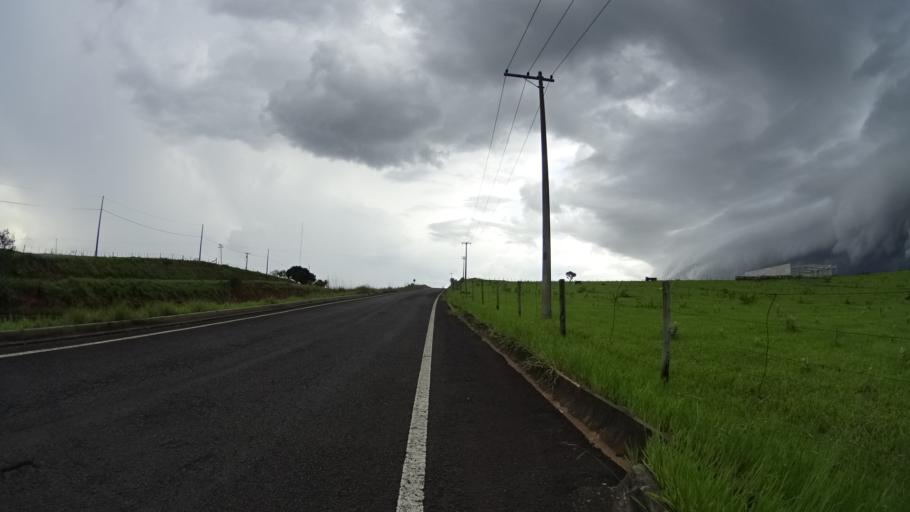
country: BR
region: Sao Paulo
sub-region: Marilia
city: Marilia
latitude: -22.2217
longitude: -49.8775
